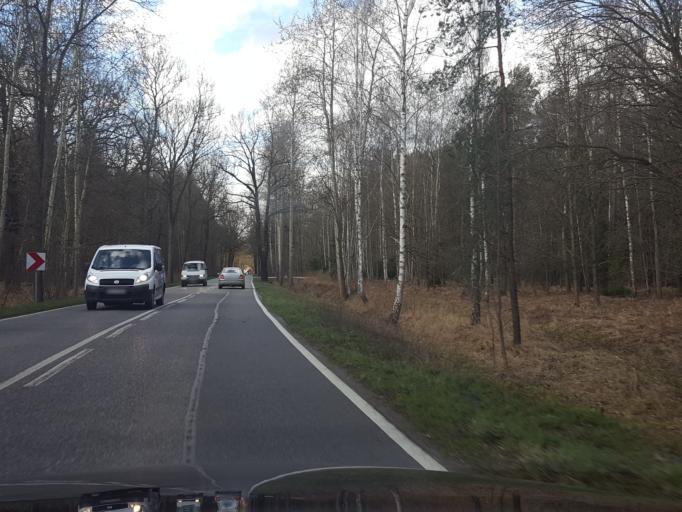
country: PL
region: Silesian Voivodeship
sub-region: Powiat mikolowski
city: Gostyn
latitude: 50.0816
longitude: 18.8949
